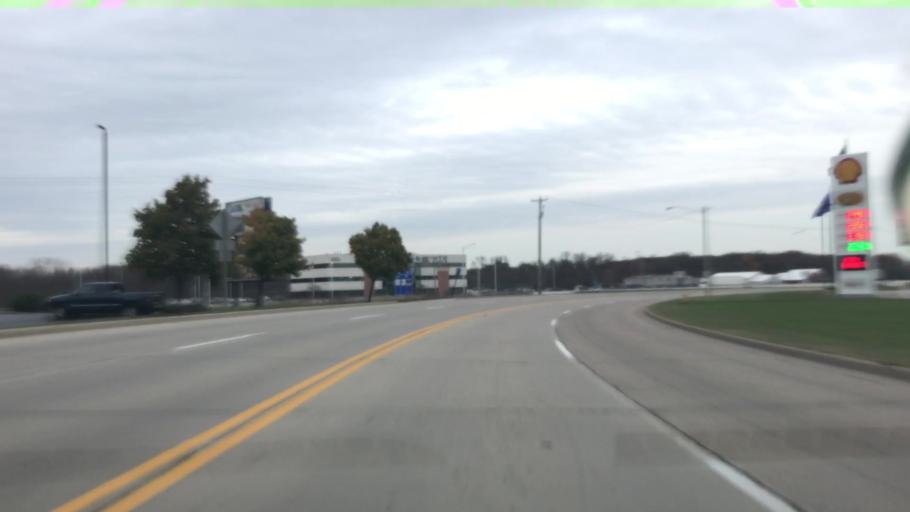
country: US
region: Wisconsin
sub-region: Brown County
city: De Pere
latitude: 44.4324
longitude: -88.1069
